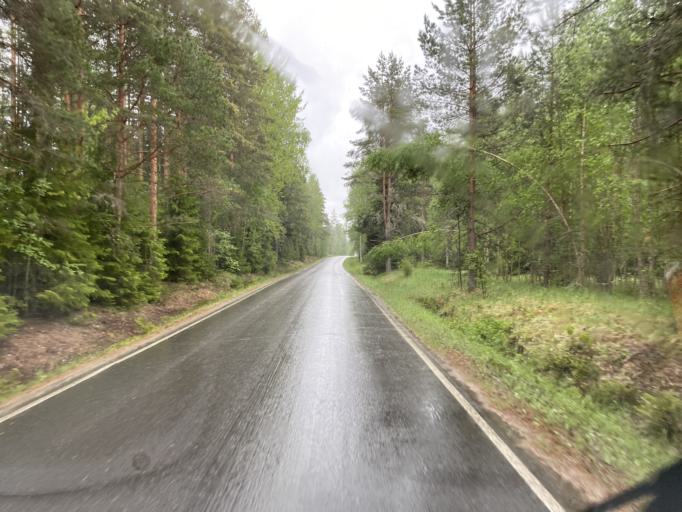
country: FI
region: Haeme
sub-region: Forssa
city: Humppila
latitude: 61.0848
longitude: 23.3102
